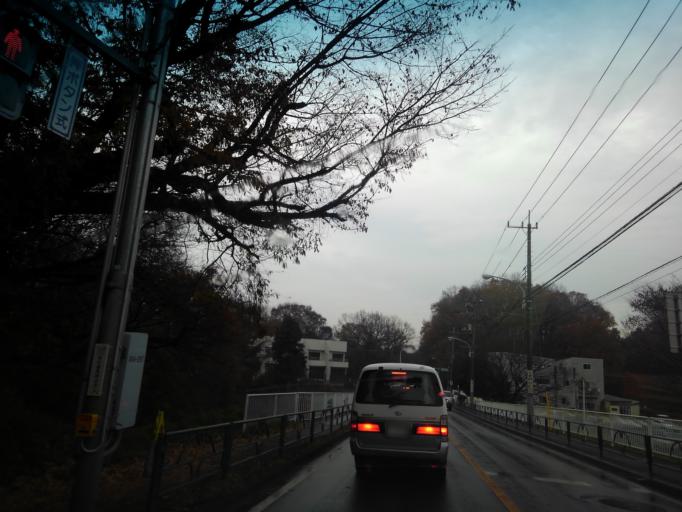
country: JP
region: Tokyo
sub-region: Machida-shi
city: Machida
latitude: 35.5759
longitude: 139.4487
